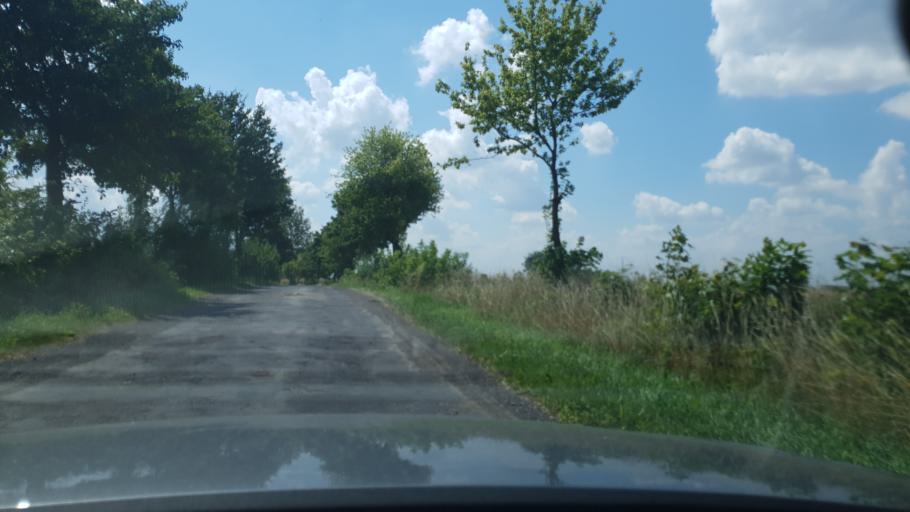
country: PL
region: Kujawsko-Pomorskie
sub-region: Powiat wabrzeski
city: Pluznica
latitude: 53.3158
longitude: 18.8231
